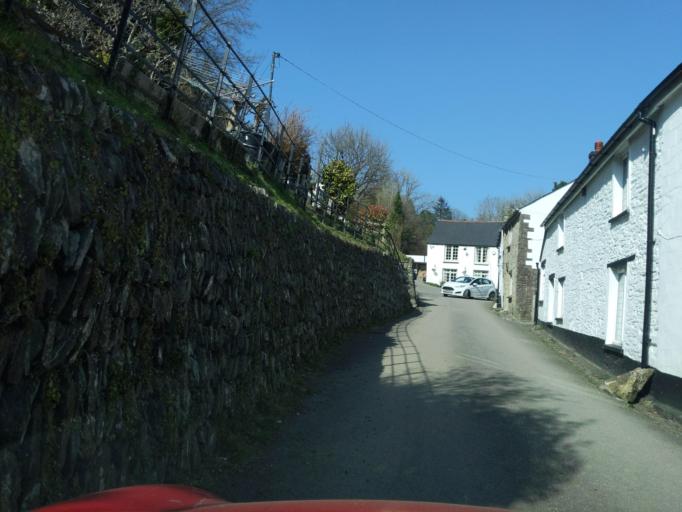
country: GB
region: England
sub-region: Devon
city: Horrabridge
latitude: 50.4748
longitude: -4.1313
